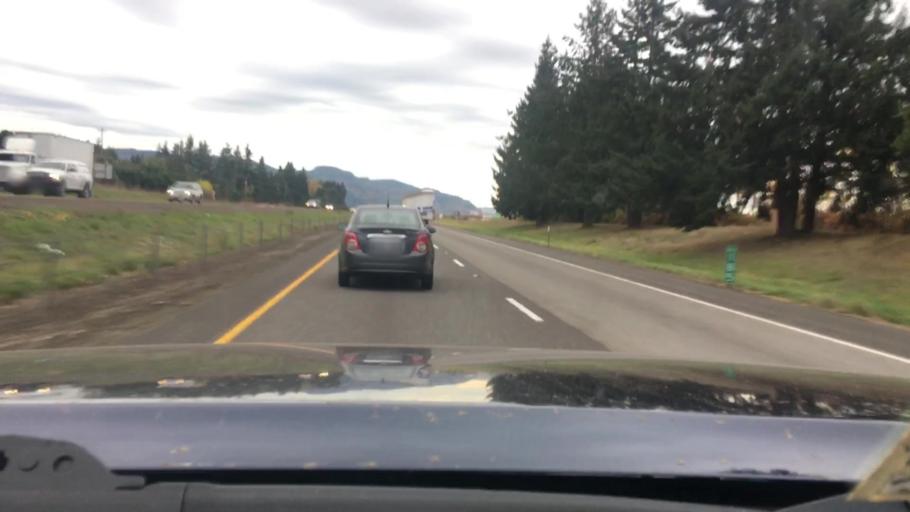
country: US
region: Oregon
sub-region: Lane County
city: Creswell
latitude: 43.9488
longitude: -123.0094
